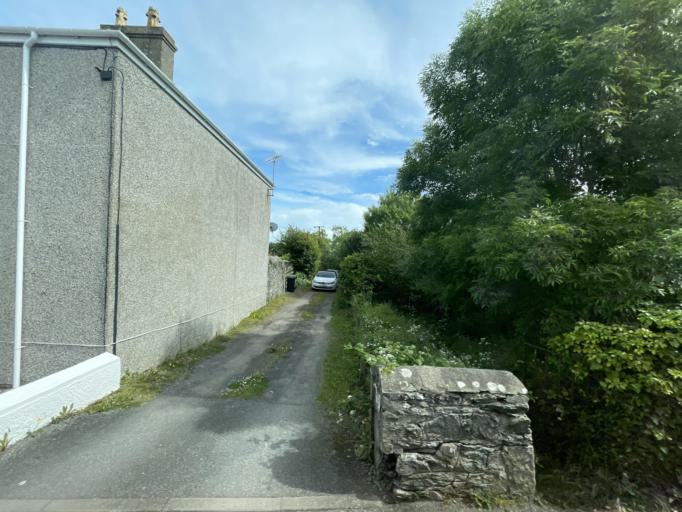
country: GB
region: Wales
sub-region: Anglesey
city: Valley
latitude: 53.2814
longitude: -4.5627
